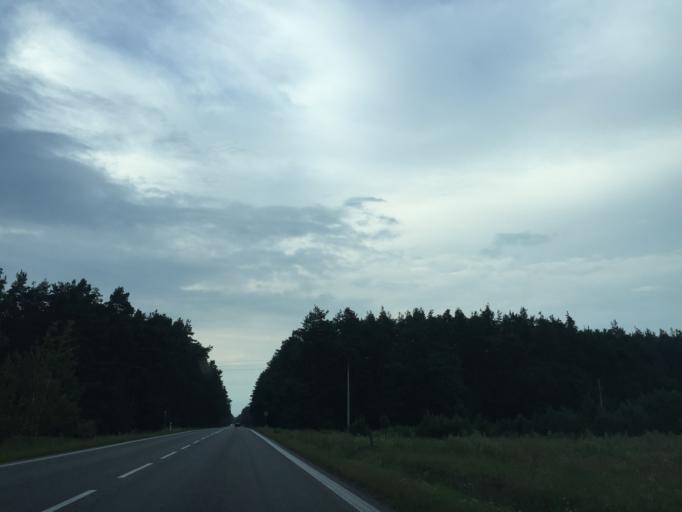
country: PL
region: Masovian Voivodeship
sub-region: Powiat ostrowski
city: Brok
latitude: 52.7531
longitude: 21.8566
